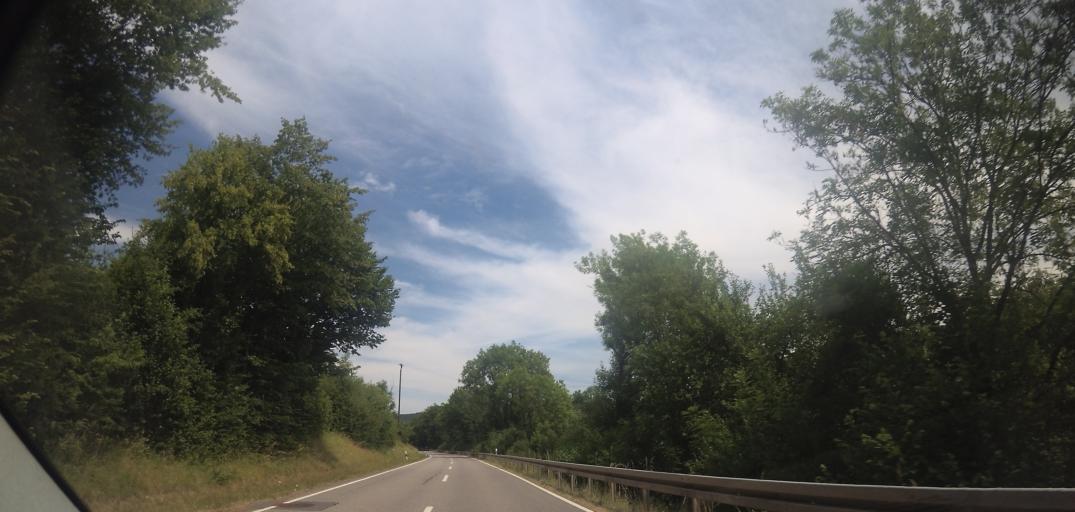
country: DE
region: Saarland
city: Merzig
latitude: 49.4171
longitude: 6.6026
